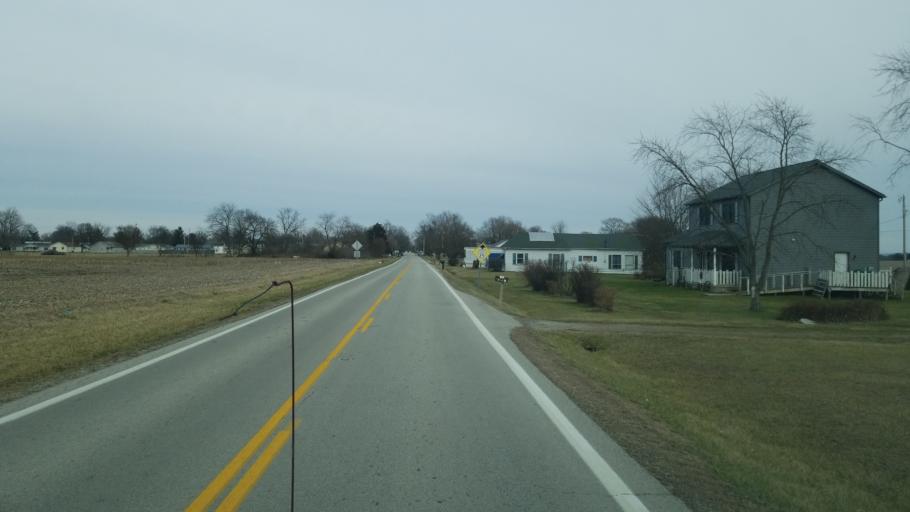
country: US
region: Ohio
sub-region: Pickaway County
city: Williamsport
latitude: 39.5033
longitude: -83.1624
